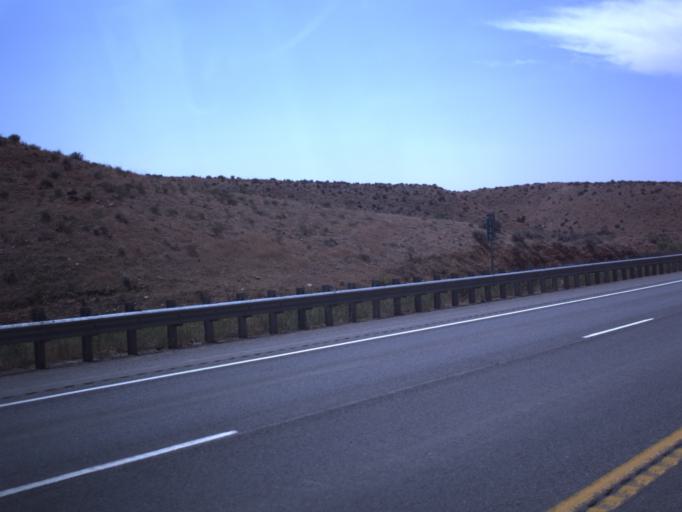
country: US
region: Utah
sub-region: Uintah County
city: Maeser
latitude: 40.3511
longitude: -109.6228
